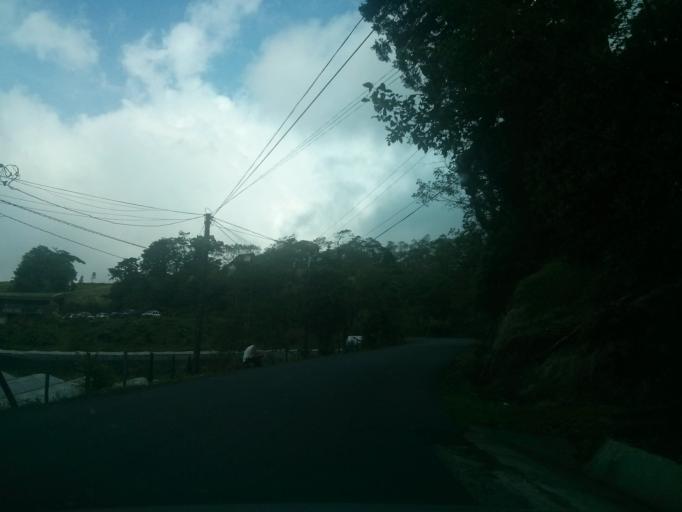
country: CR
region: Heredia
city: Santo Domingo
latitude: 10.1581
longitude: -84.1520
